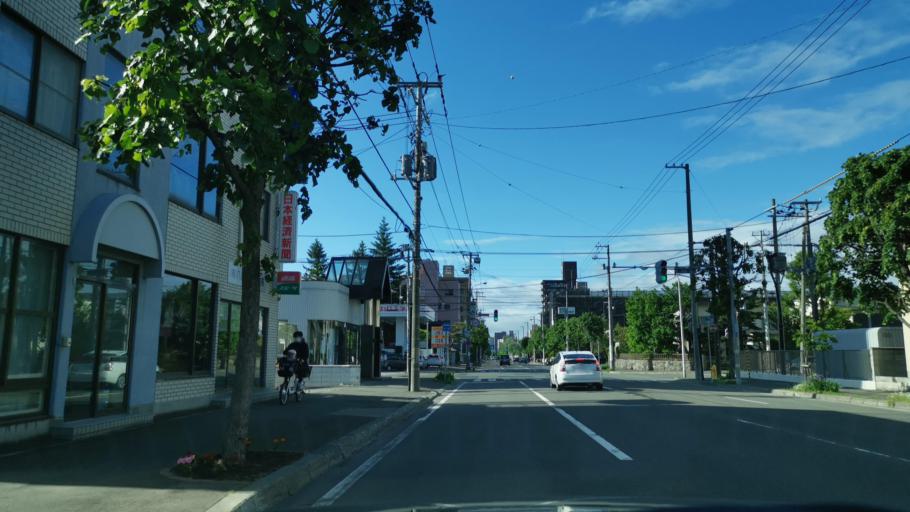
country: JP
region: Hokkaido
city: Sapporo
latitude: 43.0437
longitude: 141.3292
